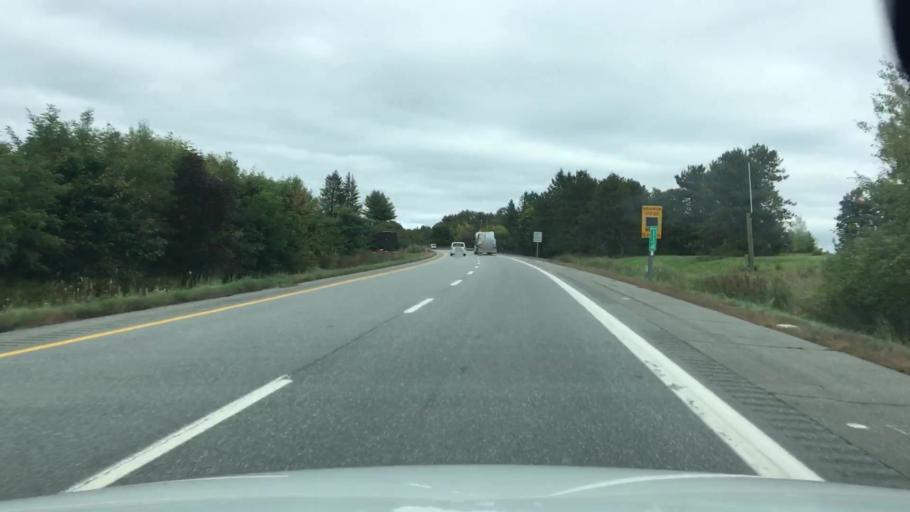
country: US
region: Maine
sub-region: Somerset County
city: Fairfield
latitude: 44.6017
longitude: -69.5867
